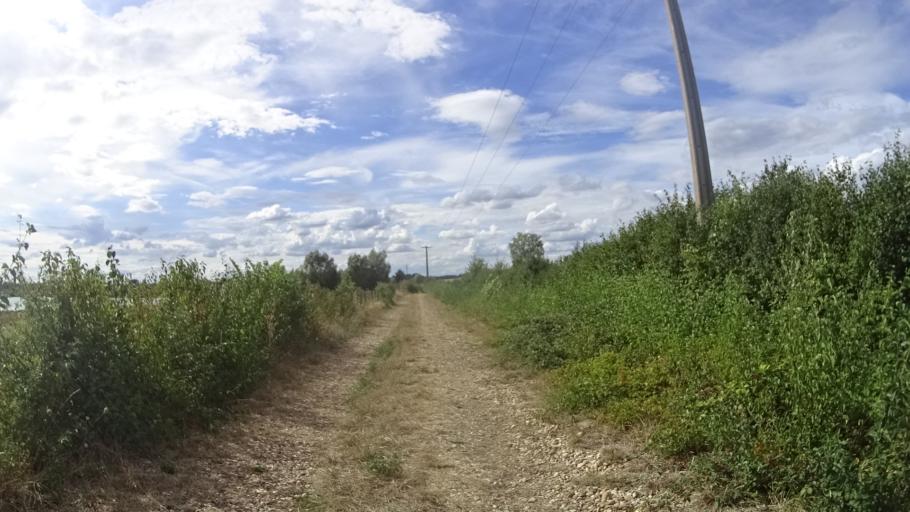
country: FR
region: Bourgogne
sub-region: Departement de la Cote-d'Or
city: Seurre
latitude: 46.9878
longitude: 5.1234
